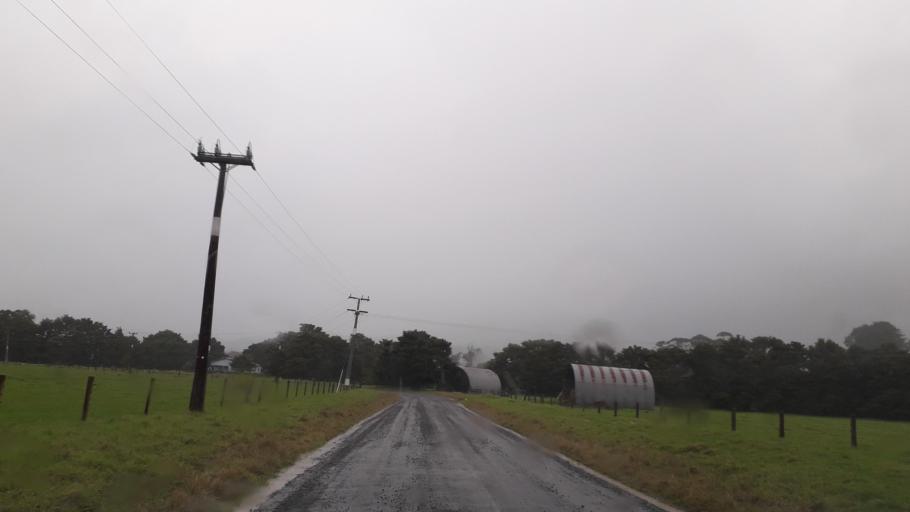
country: NZ
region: Northland
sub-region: Far North District
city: Waimate North
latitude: -35.5026
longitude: 173.6994
